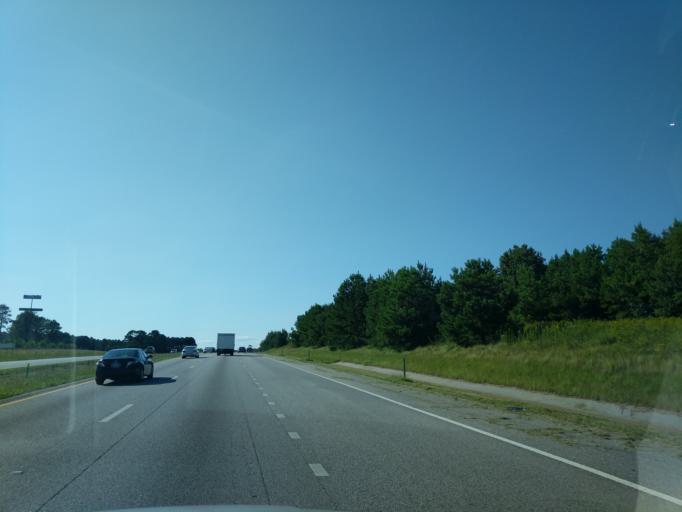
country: US
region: South Carolina
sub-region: Laurens County
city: Clinton
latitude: 34.5039
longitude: -81.8549
